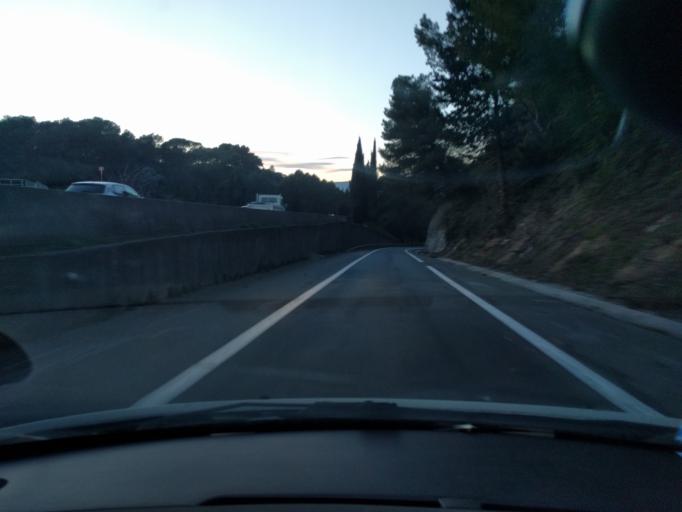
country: FR
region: Provence-Alpes-Cote d'Azur
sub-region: Departement des Alpes-Maritimes
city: Mougins
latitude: 43.6059
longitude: 6.9888
